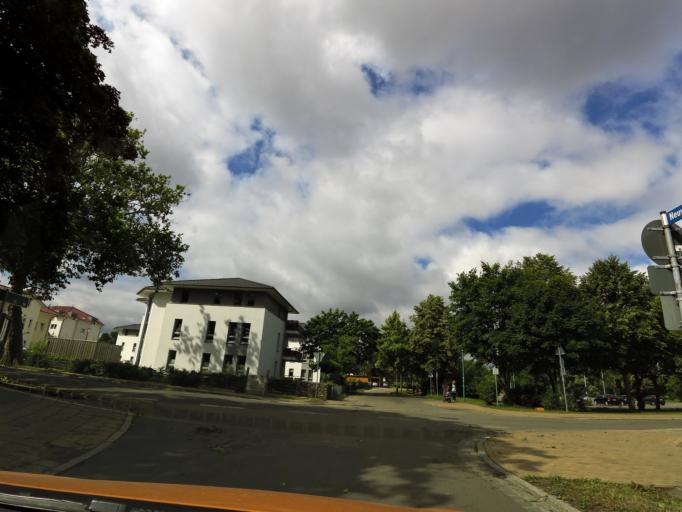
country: DE
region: Mecklenburg-Vorpommern
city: Guestrow
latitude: 53.7888
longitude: 12.1782
